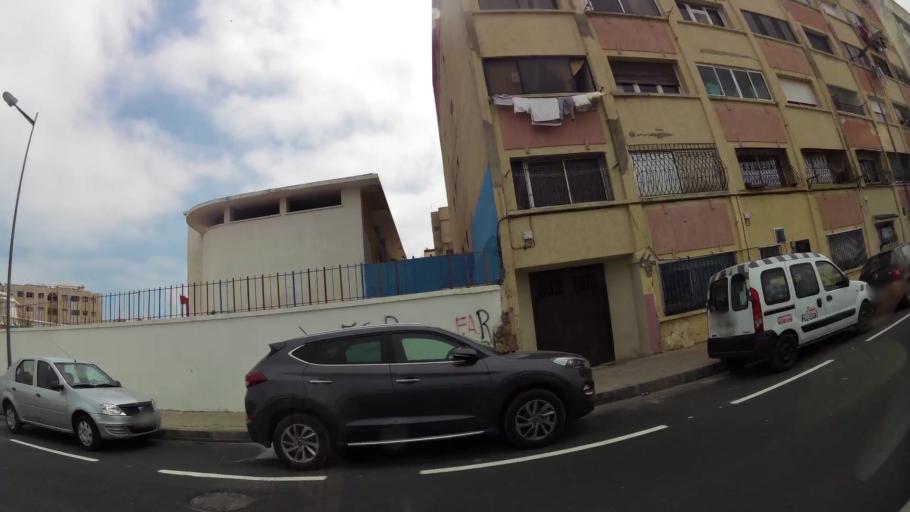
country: MA
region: Rabat-Sale-Zemmour-Zaer
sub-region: Rabat
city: Rabat
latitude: 34.0204
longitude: -6.8529
